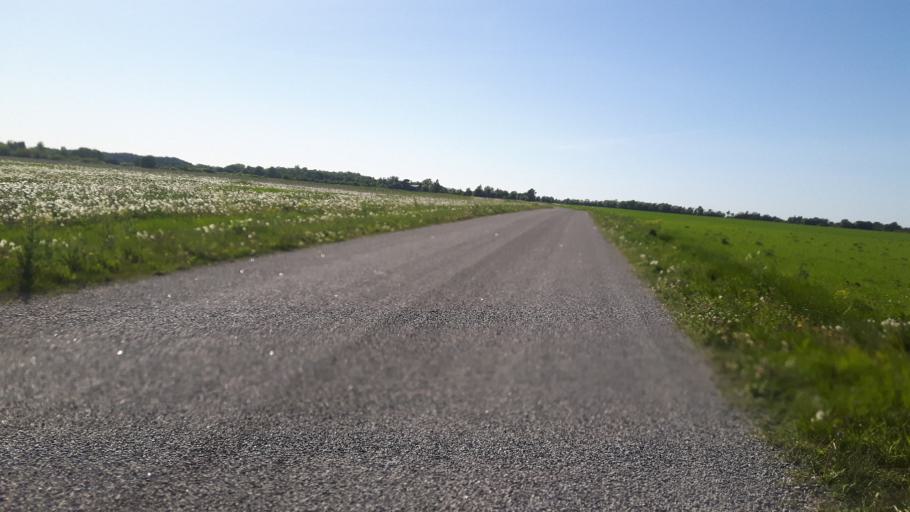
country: EE
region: Ida-Virumaa
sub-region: Kohtla-Jaerve linn
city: Kohtla-Jarve
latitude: 59.4333
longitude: 27.2101
